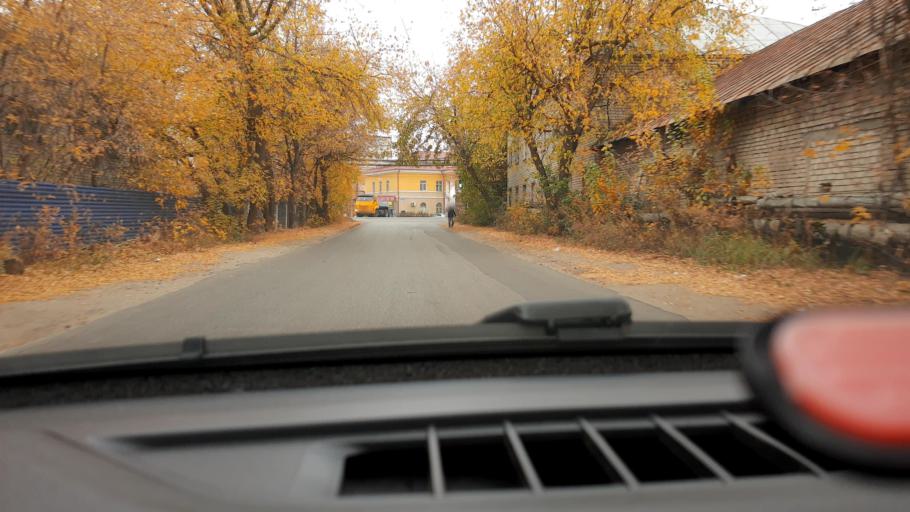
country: RU
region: Nizjnij Novgorod
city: Gorbatovka
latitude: 56.3405
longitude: 43.8192
